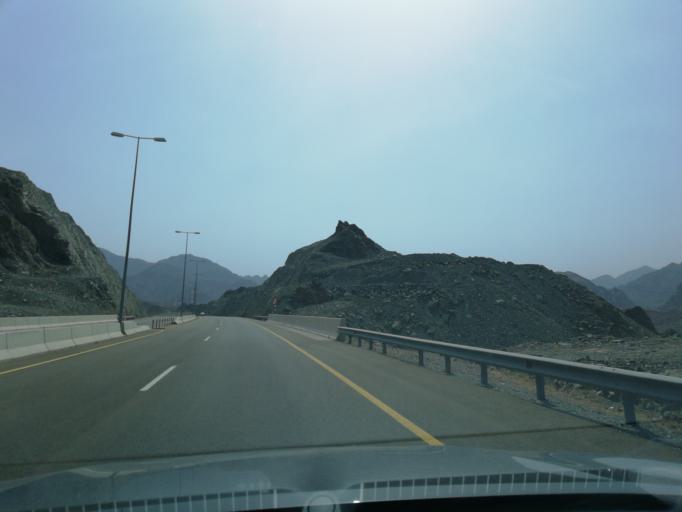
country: OM
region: Al Batinah
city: Al Liwa'
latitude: 24.2611
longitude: 56.3662
